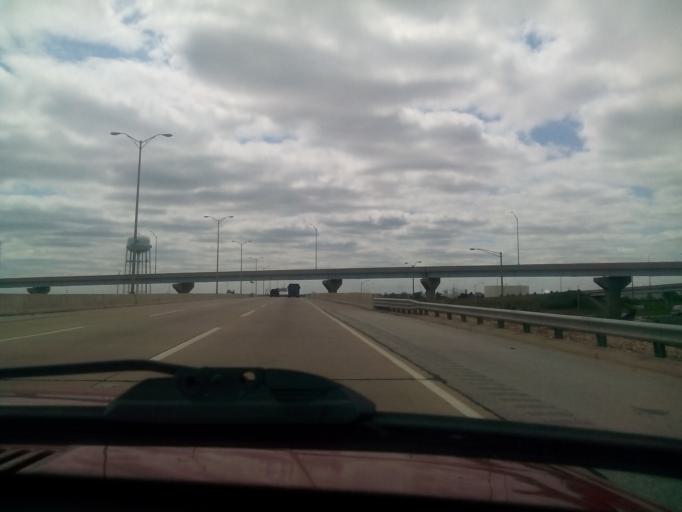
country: US
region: Illinois
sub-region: Will County
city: Bolingbrook
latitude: 41.7054
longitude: -88.0311
